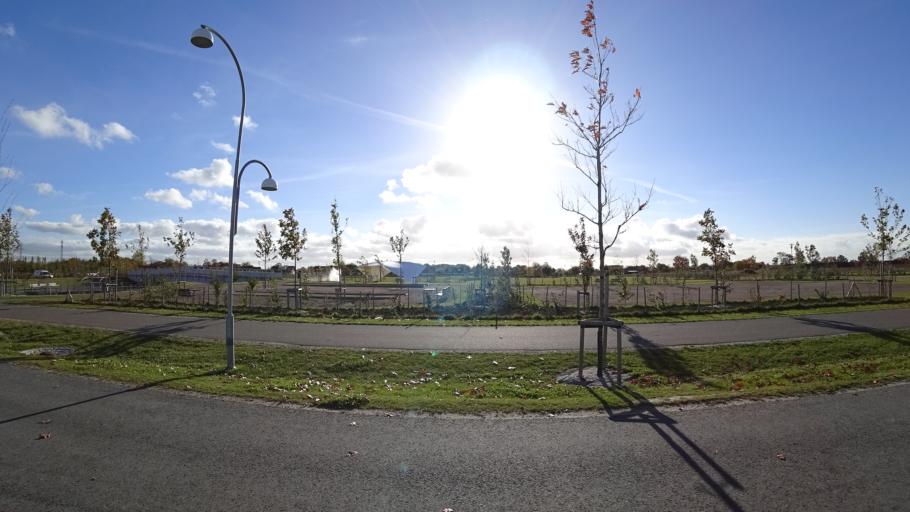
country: SE
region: Skane
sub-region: Staffanstorps Kommun
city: Hjaerup
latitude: 55.6704
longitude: 13.1517
